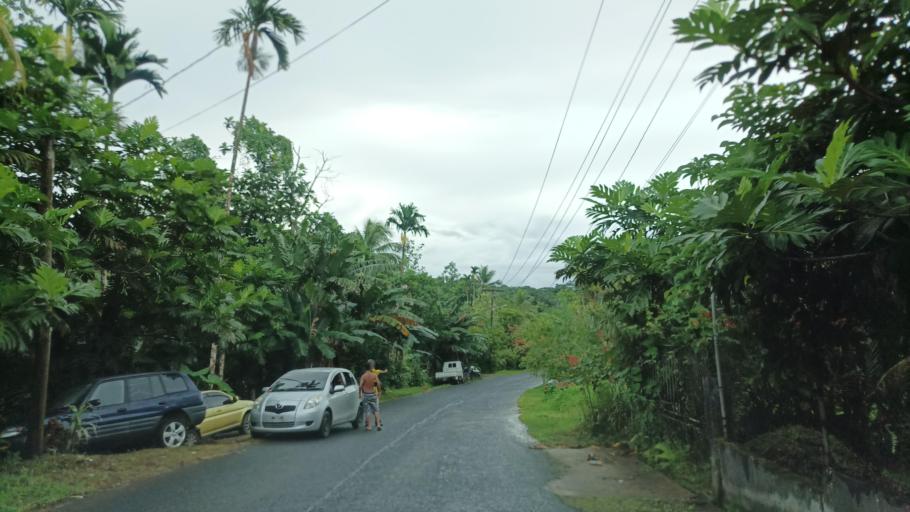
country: FM
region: Pohnpei
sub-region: Sokehs Municipality
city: Palikir - National Government Center
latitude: 6.9001
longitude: 158.1569
